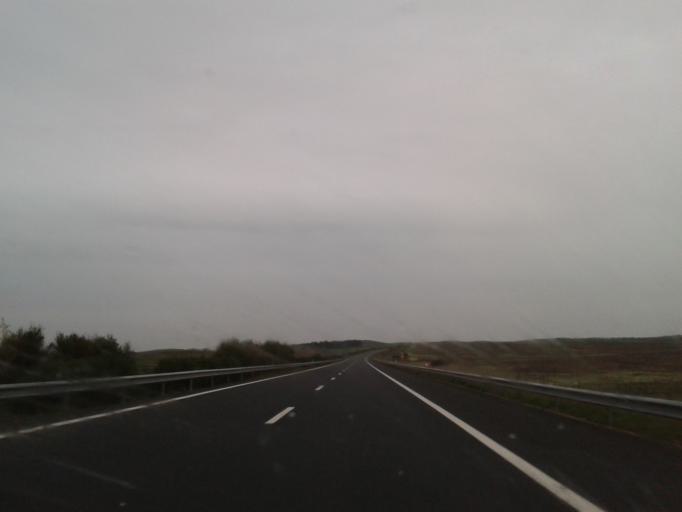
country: PT
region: Beja
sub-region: Aljustrel
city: Aljustrel
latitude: 37.7921
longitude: -8.2213
